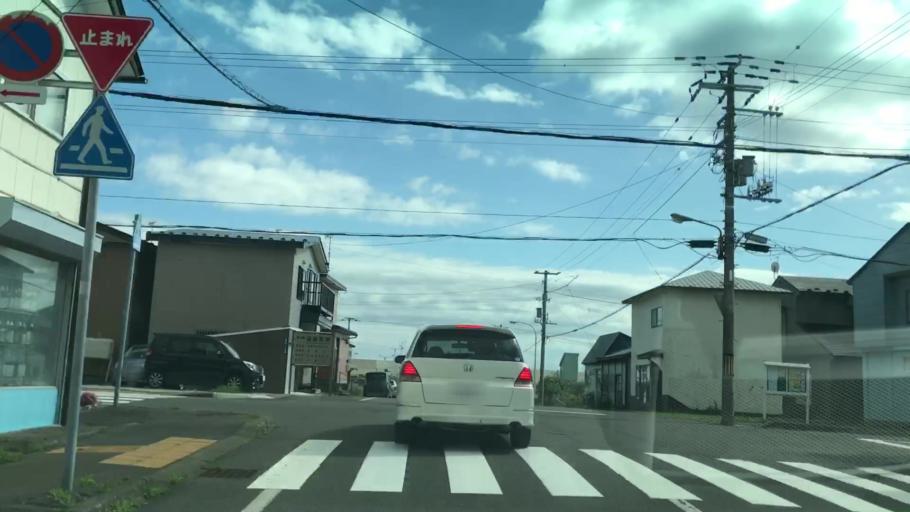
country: JP
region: Hokkaido
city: Muroran
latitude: 42.3105
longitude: 140.9729
